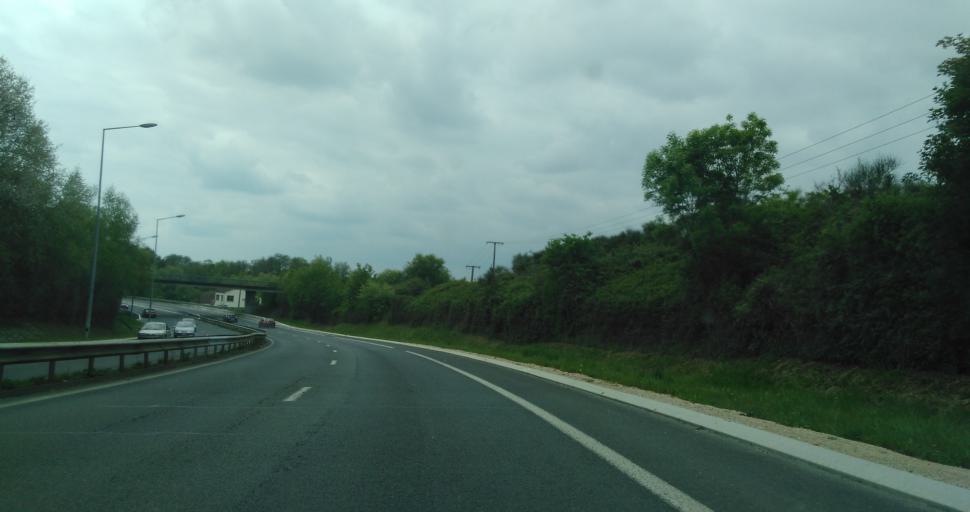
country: FR
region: Poitou-Charentes
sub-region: Departement des Deux-Sevres
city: Niort
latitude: 46.3377
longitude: -0.4617
